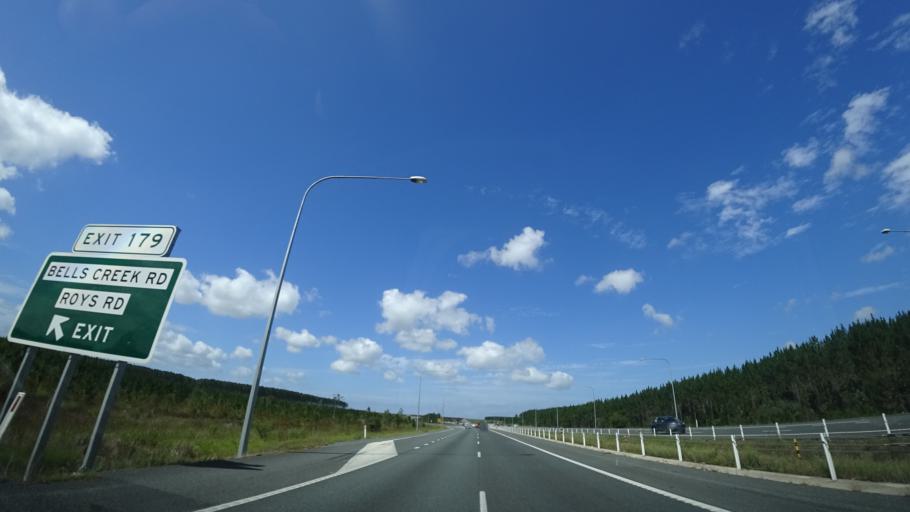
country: AU
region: Queensland
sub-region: Sunshine Coast
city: Little Mountain
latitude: -26.8569
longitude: 153.0213
